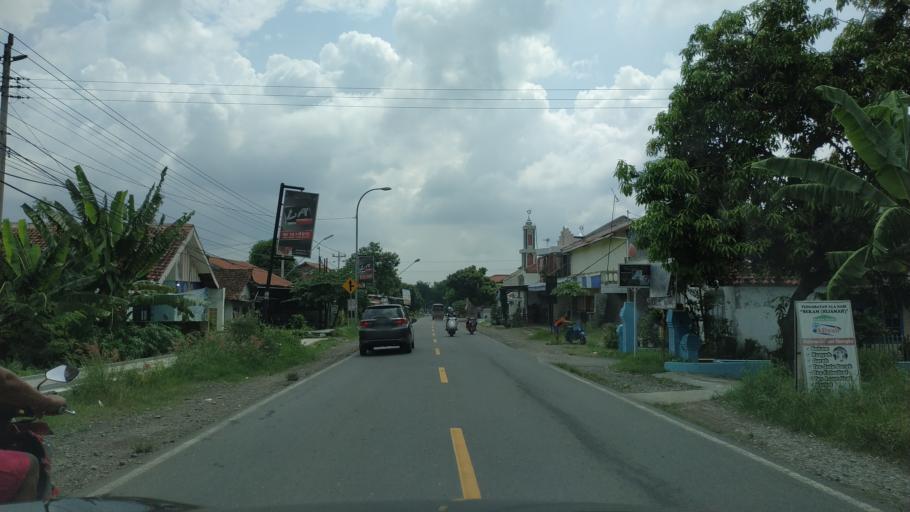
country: ID
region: Central Java
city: Lebaksiu
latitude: -7.0440
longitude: 109.1466
